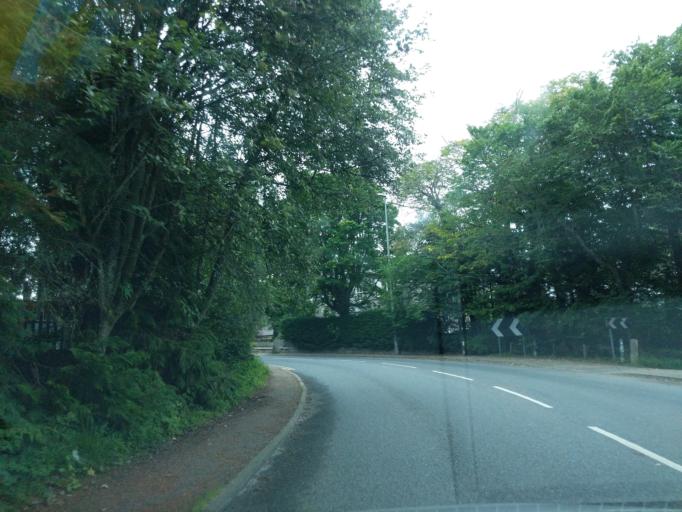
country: GB
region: Scotland
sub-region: Highland
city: Grantown on Spey
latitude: 57.3280
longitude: -3.6073
